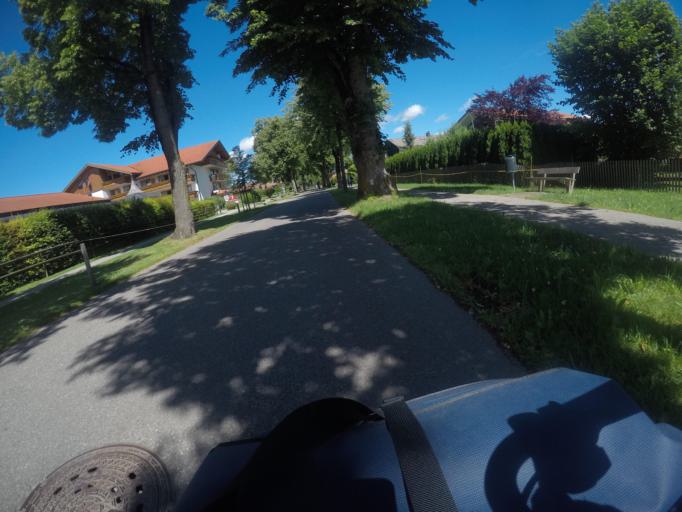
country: DE
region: Bavaria
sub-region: Swabia
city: Schwangau
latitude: 47.5814
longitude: 10.7329
